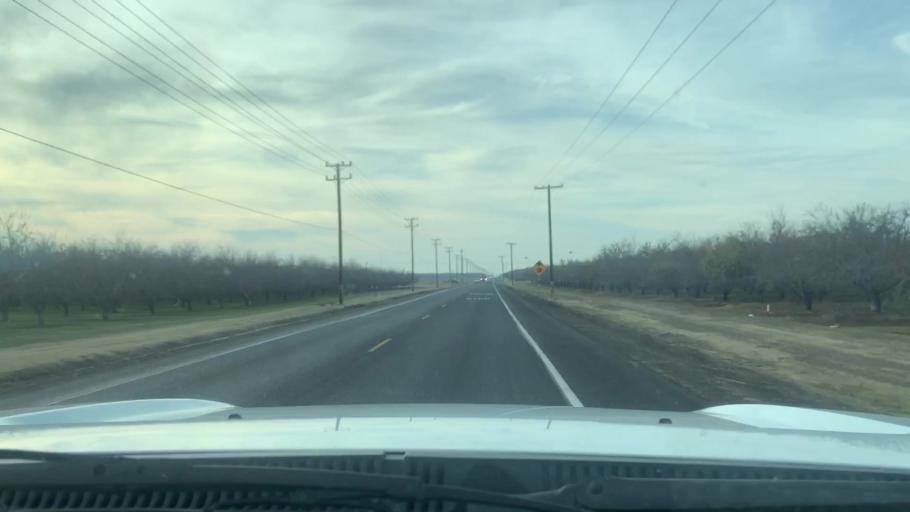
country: US
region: California
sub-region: Kern County
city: Lost Hills
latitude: 35.4992
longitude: -119.6863
